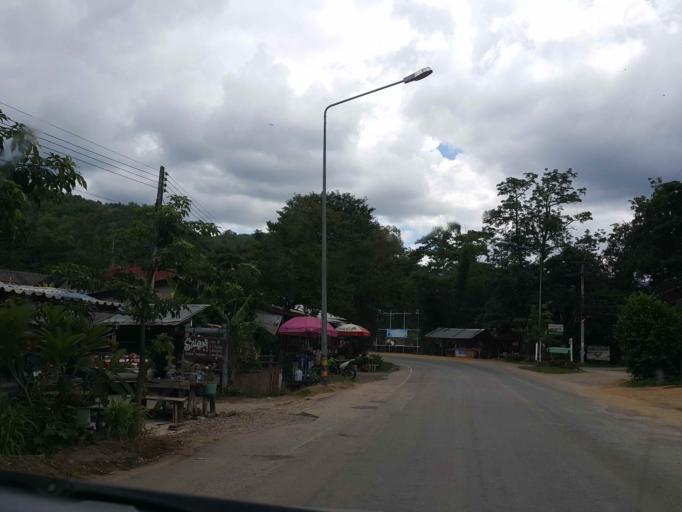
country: TH
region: Chiang Mai
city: Samoeng
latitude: 18.7939
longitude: 98.8366
